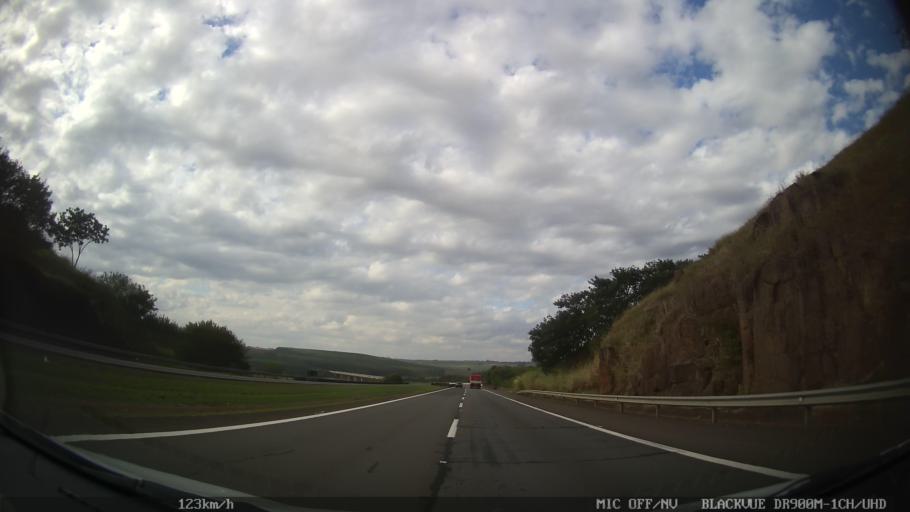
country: BR
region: Sao Paulo
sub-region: Cordeiropolis
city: Cordeiropolis
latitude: -22.5271
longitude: -47.4394
